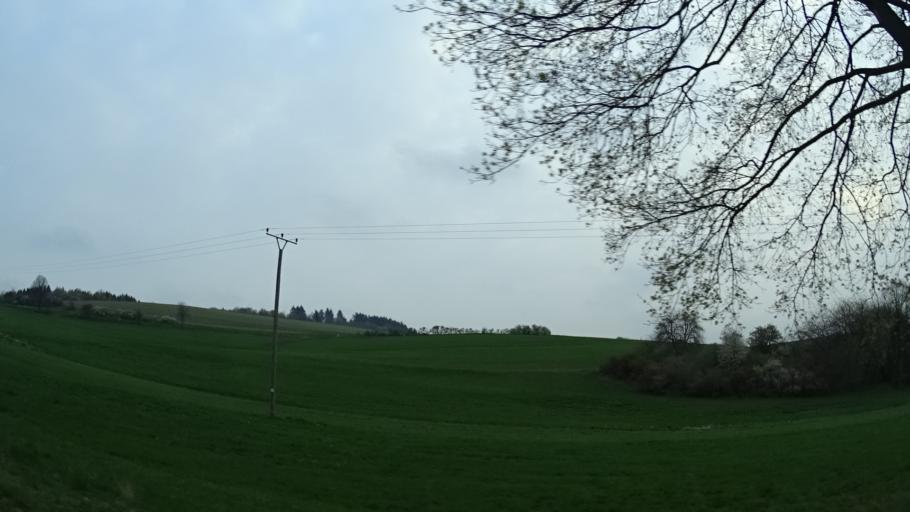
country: DE
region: Rheinland-Pfalz
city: Schmissberg
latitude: 49.6536
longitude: 7.1931
